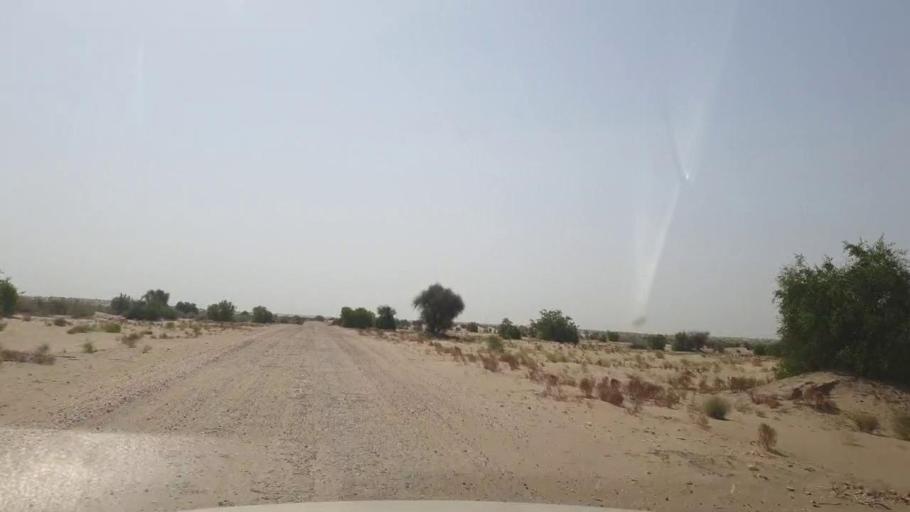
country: PK
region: Sindh
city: Khanpur
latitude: 27.4319
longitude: 69.2525
